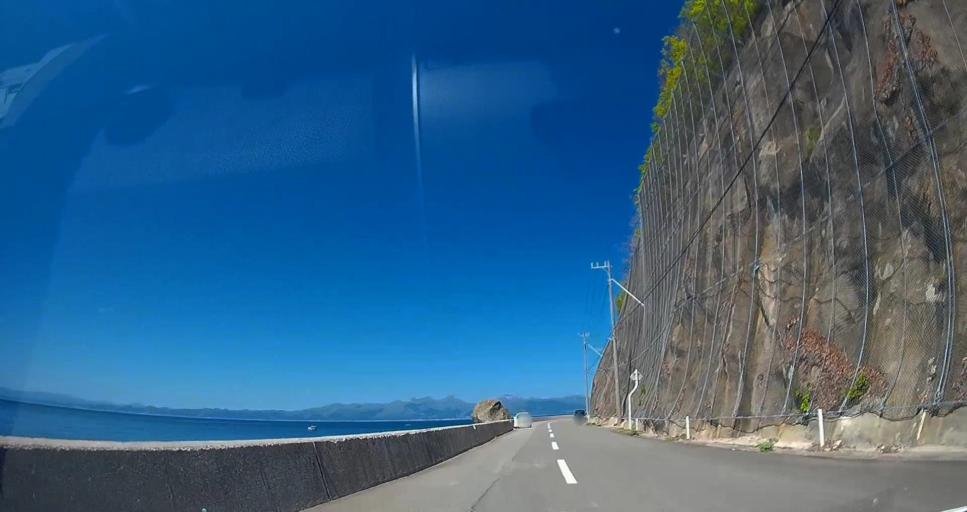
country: JP
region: Aomori
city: Aomori Shi
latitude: 41.1388
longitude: 140.7759
